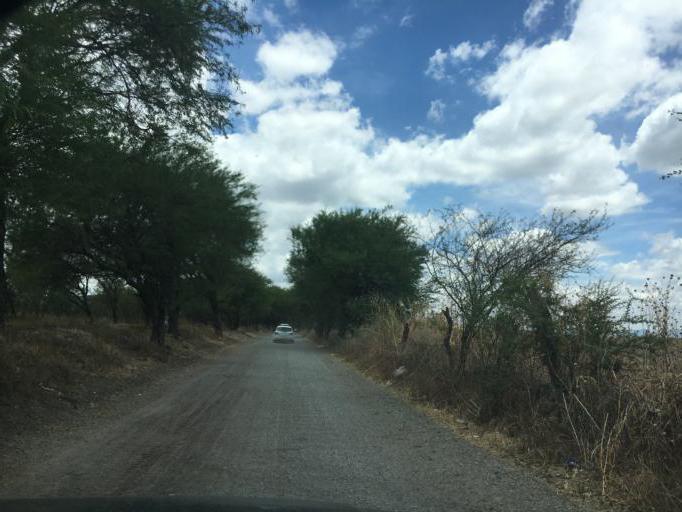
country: MX
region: Guanajuato
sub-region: Leon
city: Plan Guanajuato (La Sandia)
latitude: 20.9199
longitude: -101.7492
